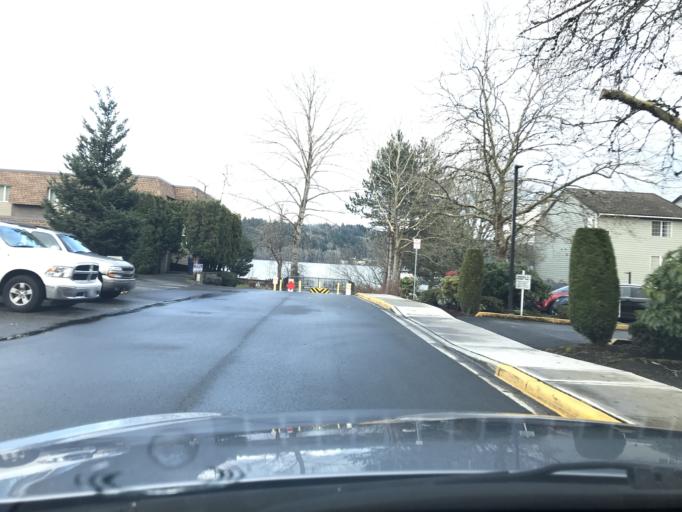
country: US
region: Washington
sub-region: King County
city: Sammamish
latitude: 47.6461
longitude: -122.1060
